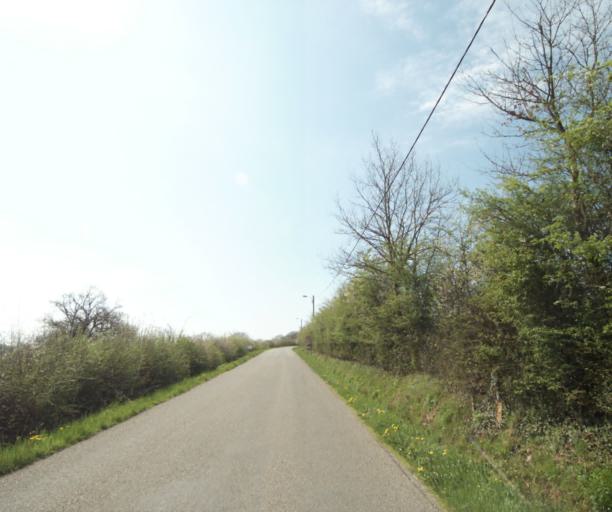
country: FR
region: Bourgogne
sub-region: Departement de Saone-et-Loire
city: Palinges
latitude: 46.5539
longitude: 4.2018
